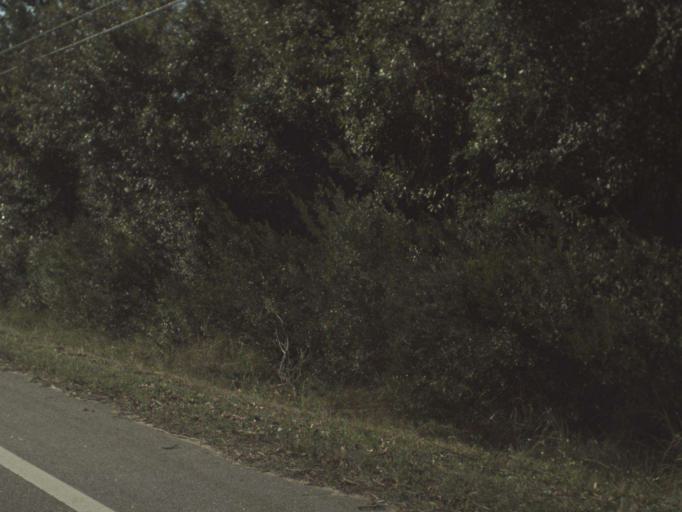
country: US
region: Florida
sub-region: Escambia County
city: Myrtle Grove
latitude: 30.3669
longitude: -87.3398
